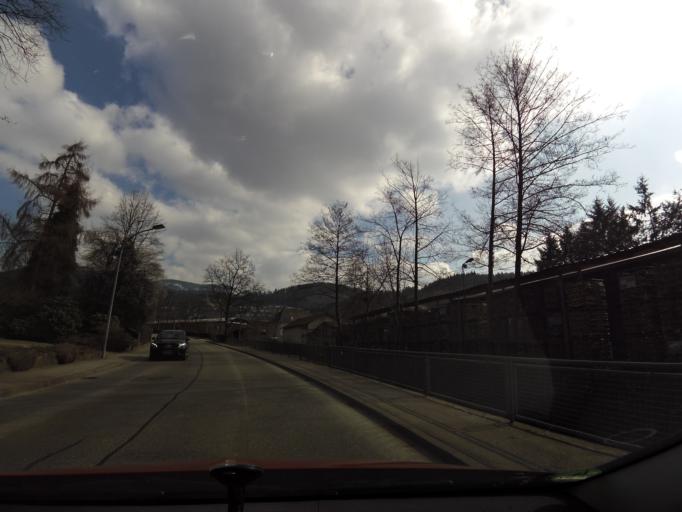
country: DE
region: Baden-Wuerttemberg
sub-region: Freiburg Region
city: Ottenhofen im Schwarzwald
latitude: 48.5674
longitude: 8.1441
